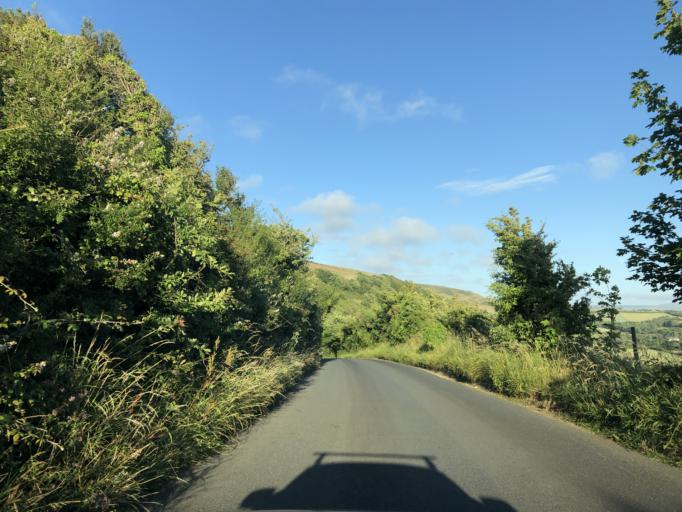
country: GB
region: England
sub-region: Isle of Wight
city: Shalfleet
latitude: 50.6578
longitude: -1.4049
